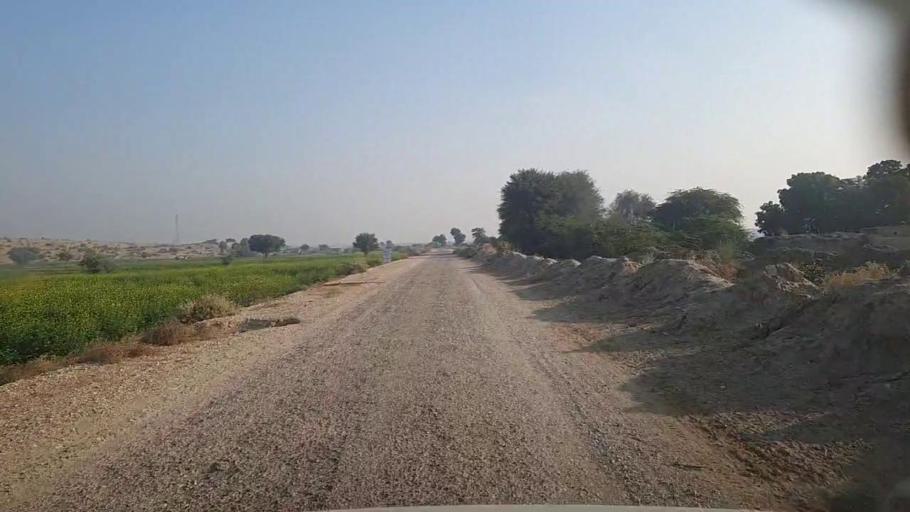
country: PK
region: Sindh
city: Karaundi
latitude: 26.7252
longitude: 68.4890
